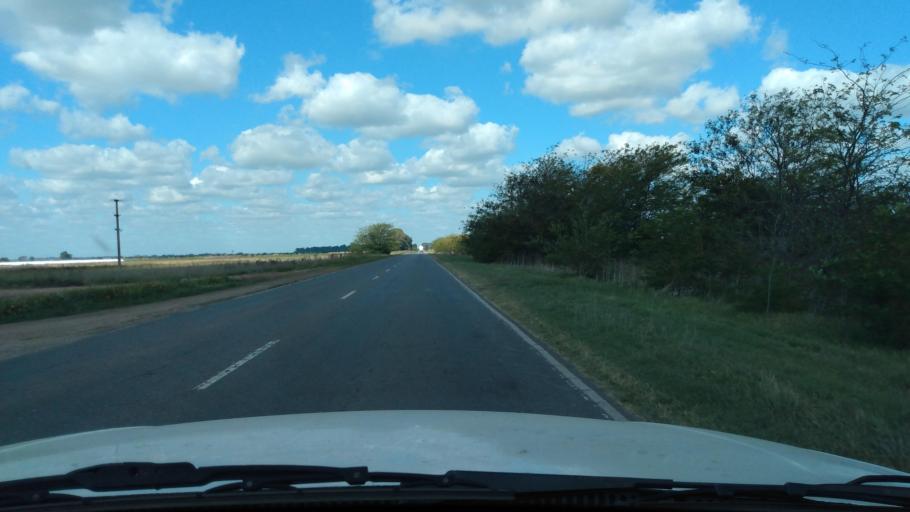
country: AR
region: Buenos Aires
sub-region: Partido de Navarro
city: Navarro
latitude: -34.9699
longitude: -59.3175
